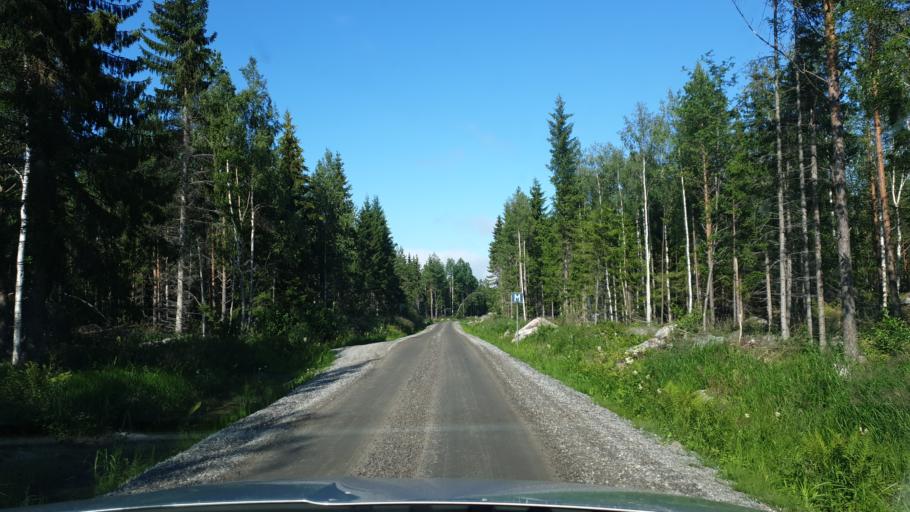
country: SE
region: Gaevleborg
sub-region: Soderhamns Kommun
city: Soderhamn
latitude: 61.4504
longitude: 17.0605
